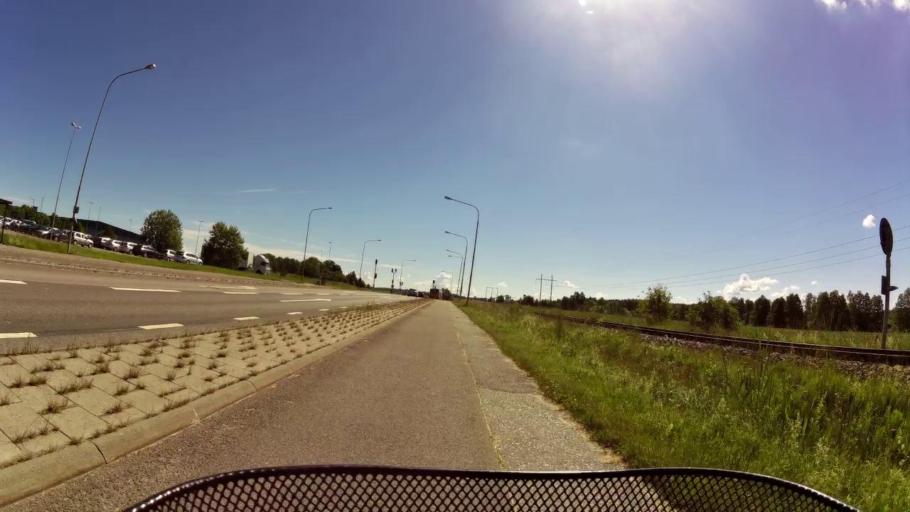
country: SE
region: OEstergoetland
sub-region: Linkopings Kommun
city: Linkoping
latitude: 58.4001
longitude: 15.6737
